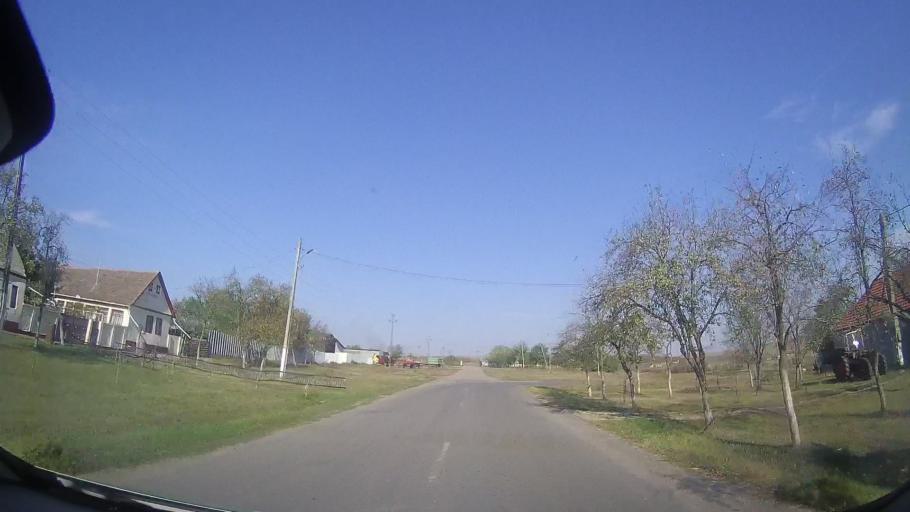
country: RO
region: Timis
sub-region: Comuna Topolovatu Mare
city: Topolovatu Mare
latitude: 45.8187
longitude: 21.5785
